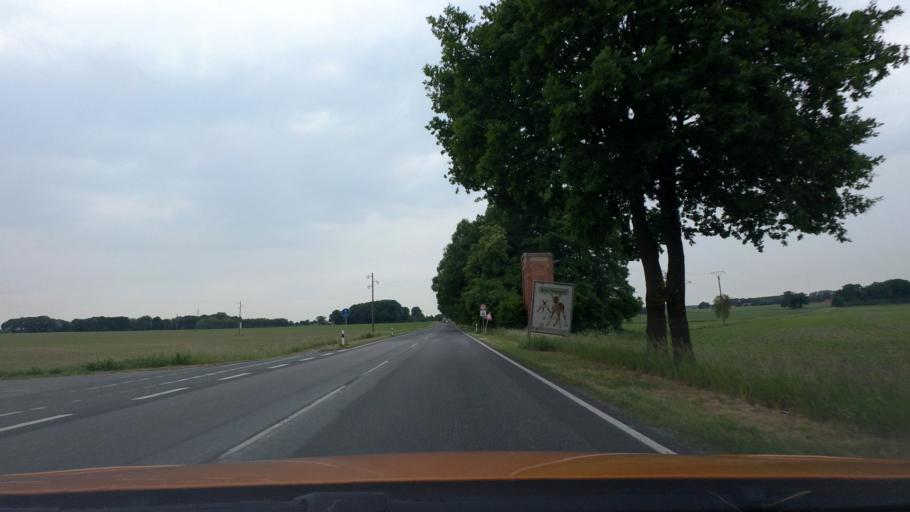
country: DE
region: Lower Saxony
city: Wietzen
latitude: 52.7289
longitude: 9.0414
